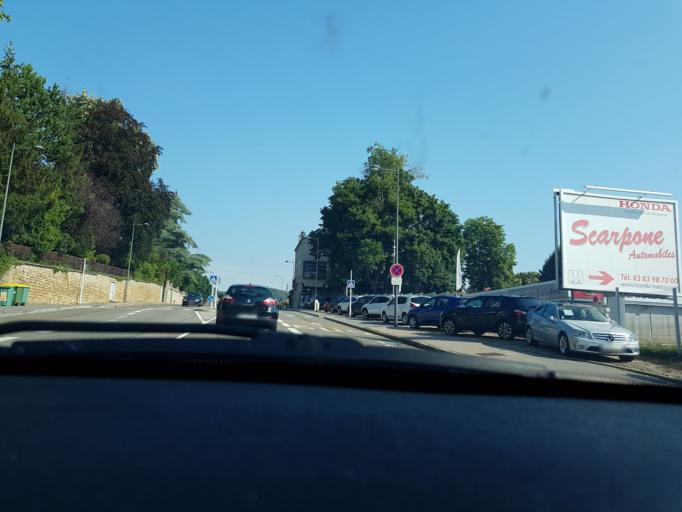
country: FR
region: Lorraine
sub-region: Departement de Meurthe-et-Moselle
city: Maxeville
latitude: 48.7014
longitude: 6.1642
